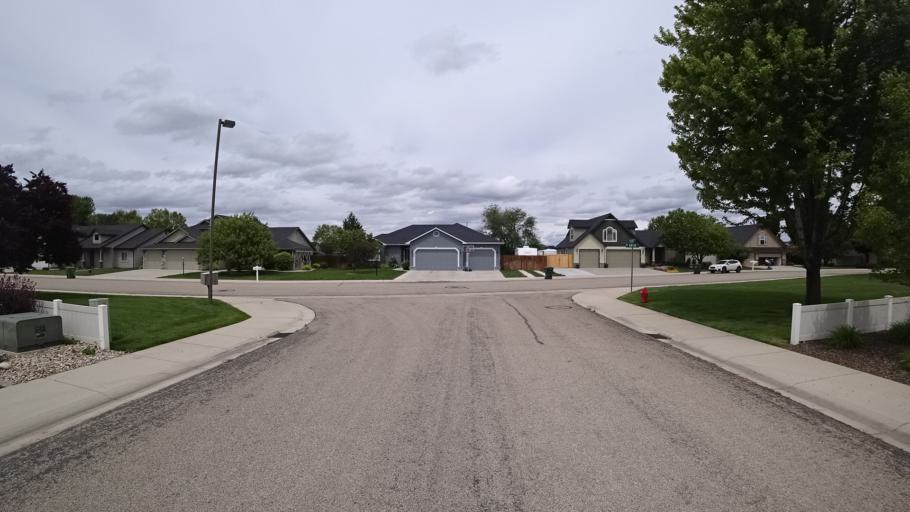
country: US
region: Idaho
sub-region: Ada County
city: Meridian
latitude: 43.6403
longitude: -116.3990
